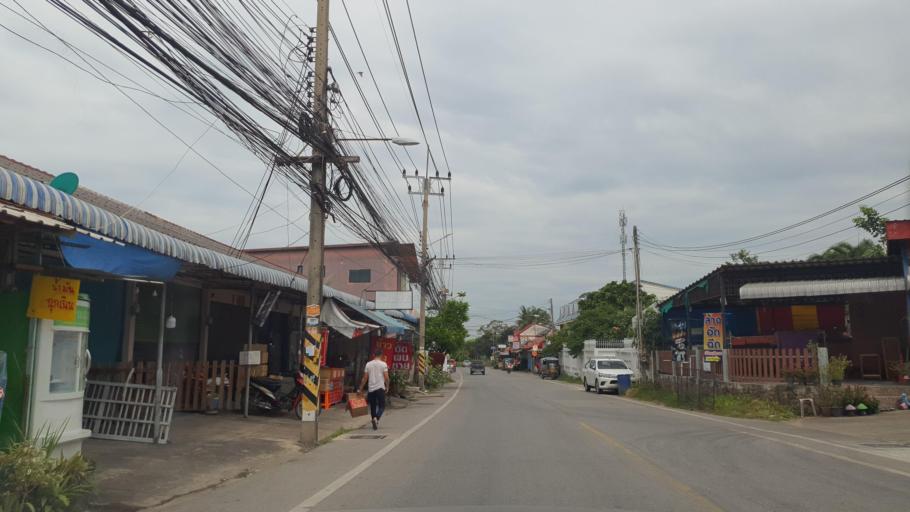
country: TH
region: Chon Buri
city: Bang Lamung
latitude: 12.9833
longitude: 100.9398
